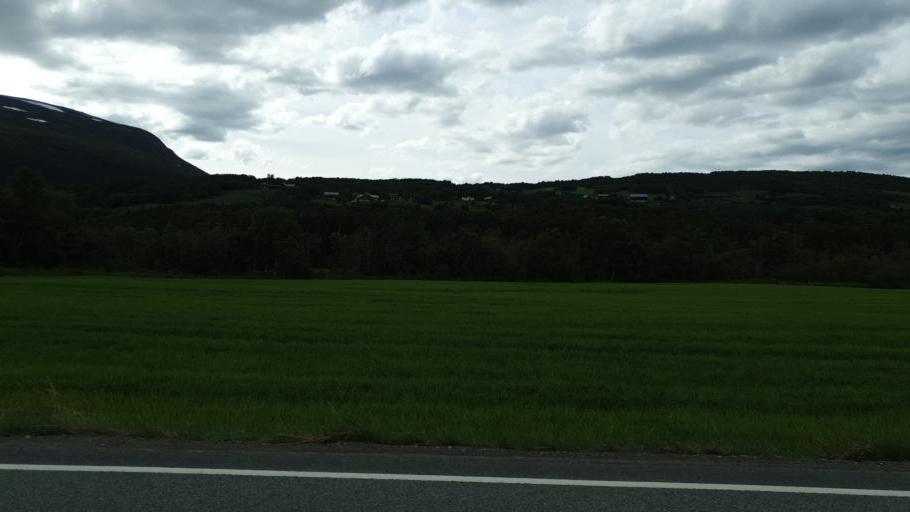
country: NO
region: Sor-Trondelag
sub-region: Oppdal
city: Oppdal
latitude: 62.5598
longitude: 9.6383
